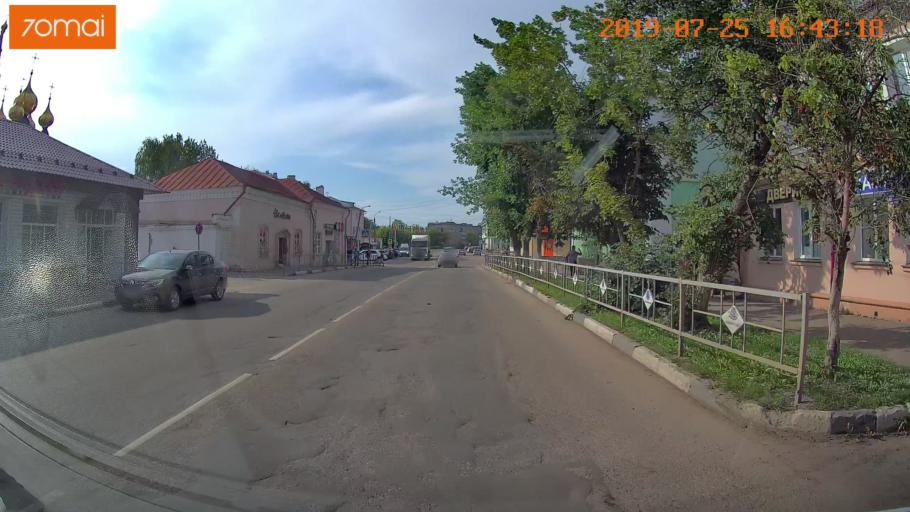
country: RU
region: Ivanovo
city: Privolzhsk
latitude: 57.3789
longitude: 41.2840
